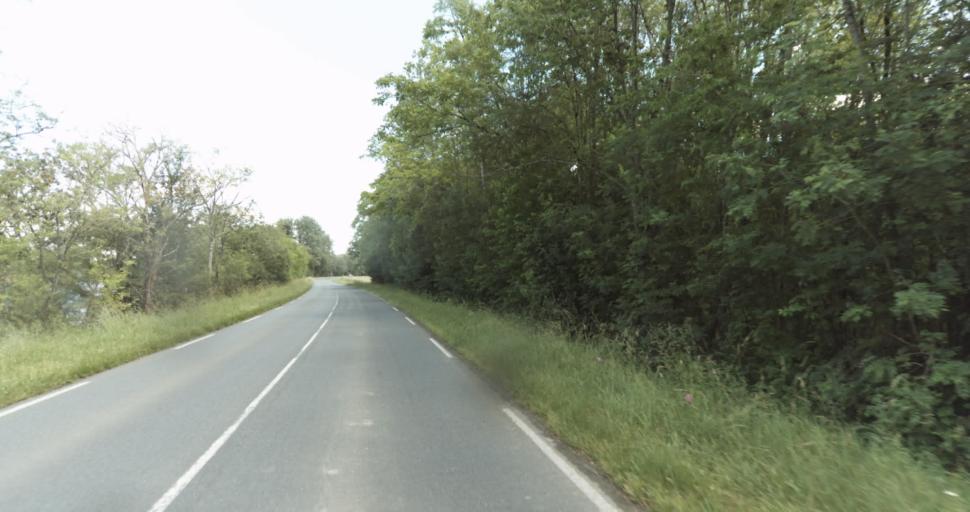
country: FR
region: Aquitaine
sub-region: Departement de la Dordogne
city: Lalinde
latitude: 44.8364
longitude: 0.7575
